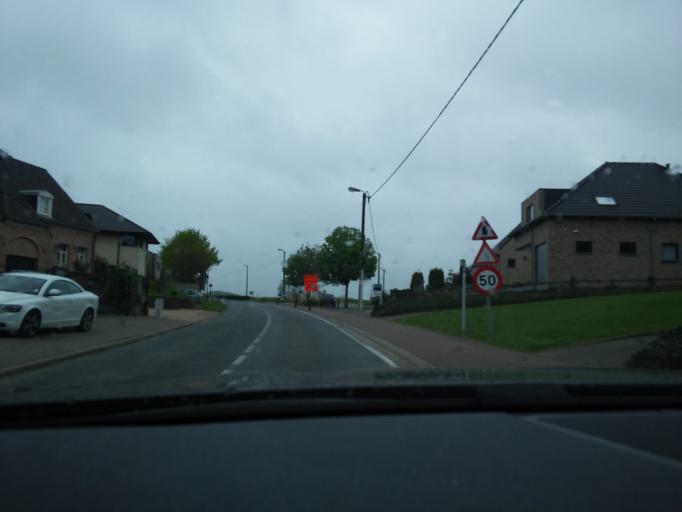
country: BE
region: Flanders
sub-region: Provincie Vlaams-Brabant
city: Pepingen
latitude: 50.7771
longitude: 4.1680
